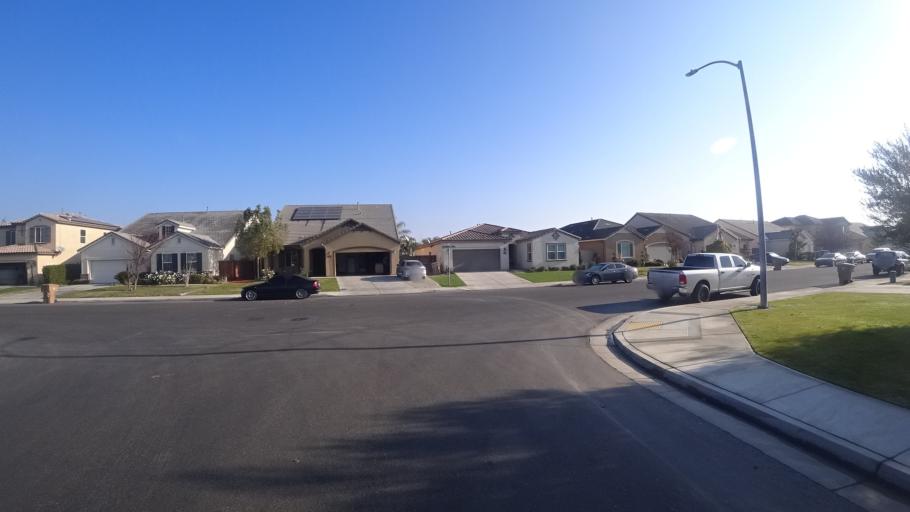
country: US
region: California
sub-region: Kern County
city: Greenacres
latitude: 35.3012
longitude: -119.1152
